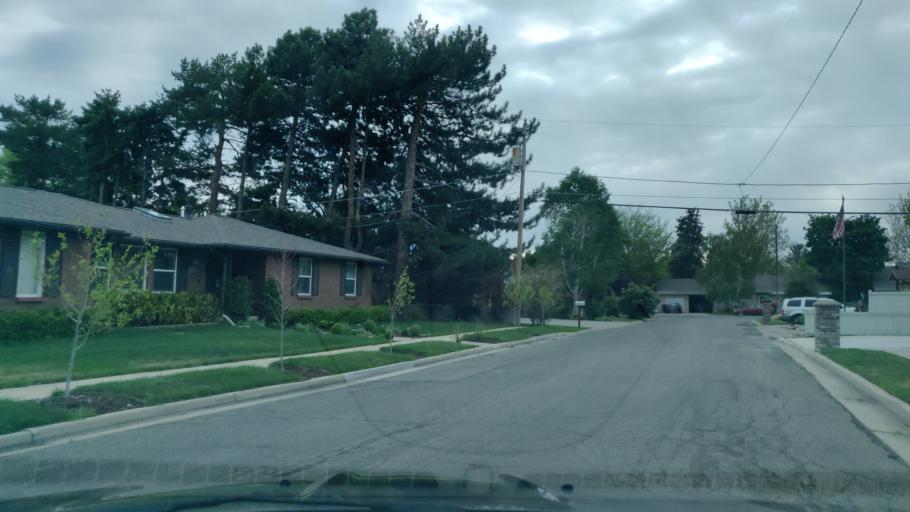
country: US
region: Utah
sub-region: Salt Lake County
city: Little Cottonwood Creek Valley
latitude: 40.6105
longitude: -111.8221
